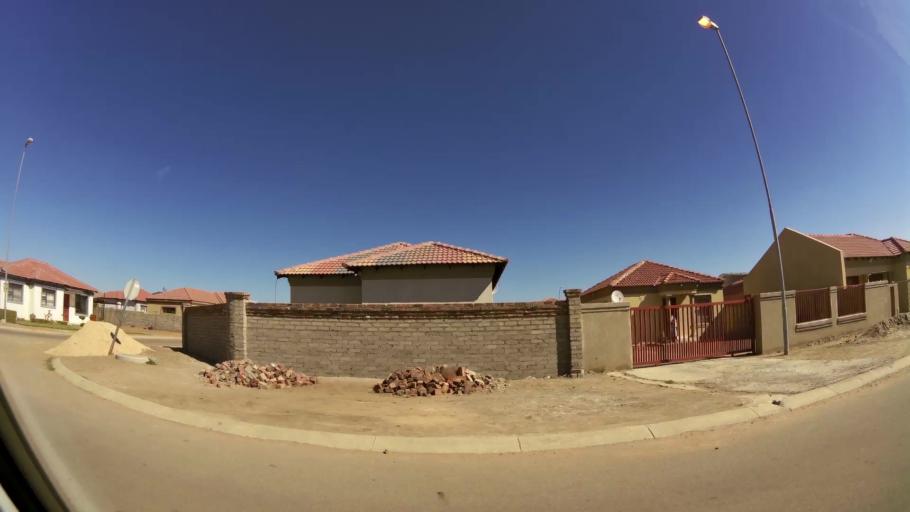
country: ZA
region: Limpopo
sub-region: Capricorn District Municipality
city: Polokwane
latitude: -23.8645
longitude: 29.4265
